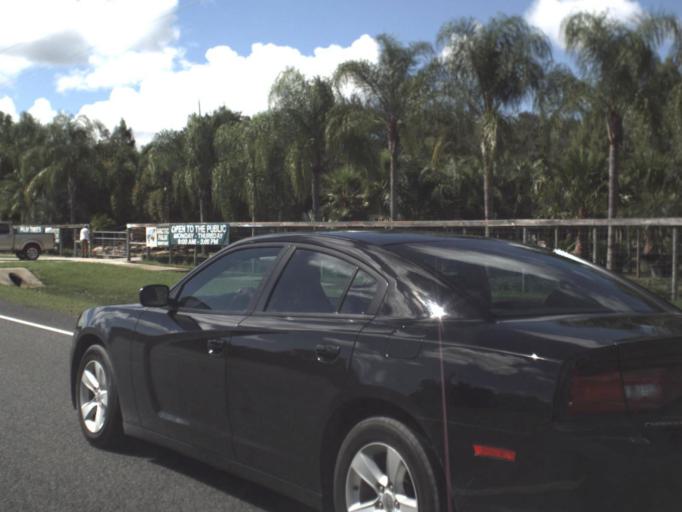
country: US
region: Florida
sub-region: Sarasota County
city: The Meadows
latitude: 27.4320
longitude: -82.3984
